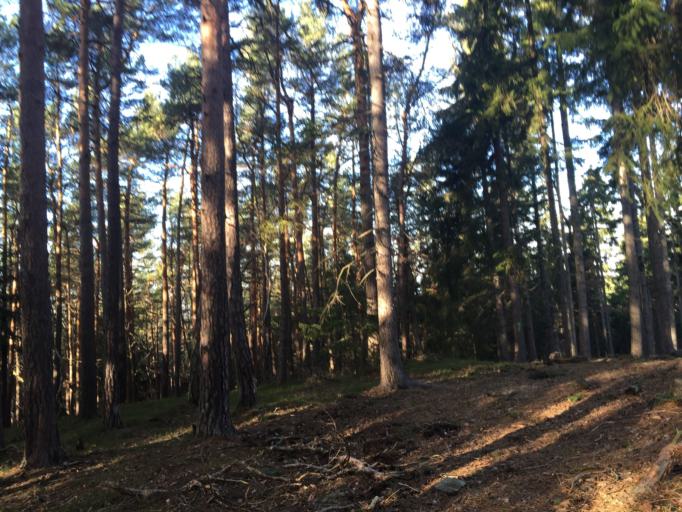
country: DE
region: Thuringia
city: Bad Blankenburg
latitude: 50.6622
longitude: 11.2715
